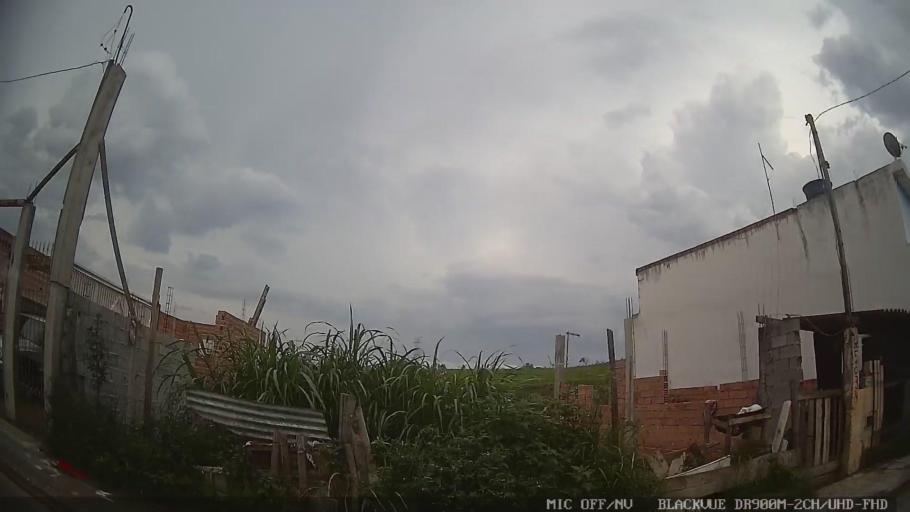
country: BR
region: Sao Paulo
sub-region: Aruja
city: Aruja
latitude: -23.4497
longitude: -46.2931
